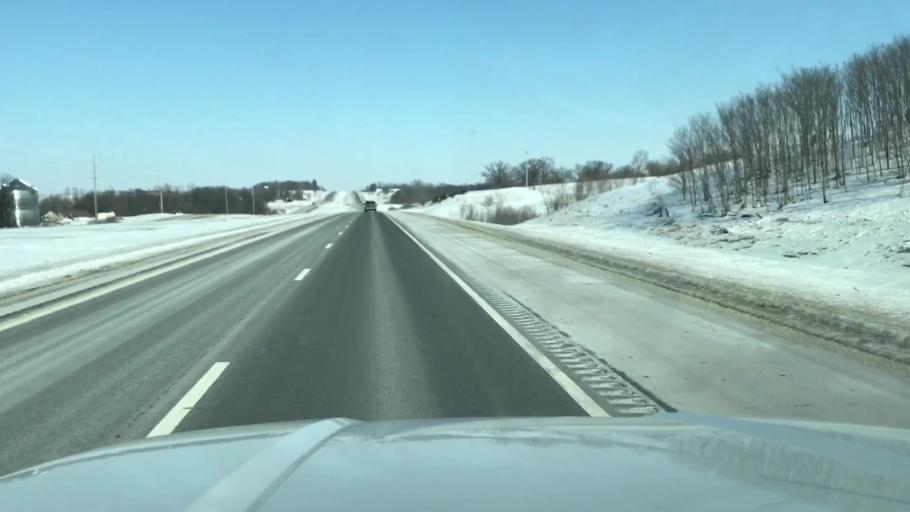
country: US
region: Missouri
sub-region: Nodaway County
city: Maryville
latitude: 40.1922
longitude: -94.8677
